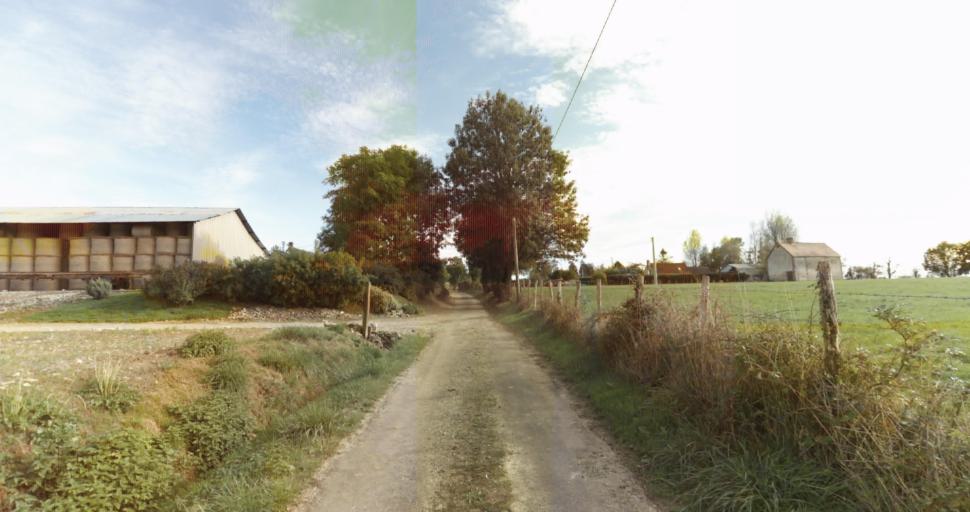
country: FR
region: Lower Normandy
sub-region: Departement de l'Orne
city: Gace
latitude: 48.7091
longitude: 0.2776
